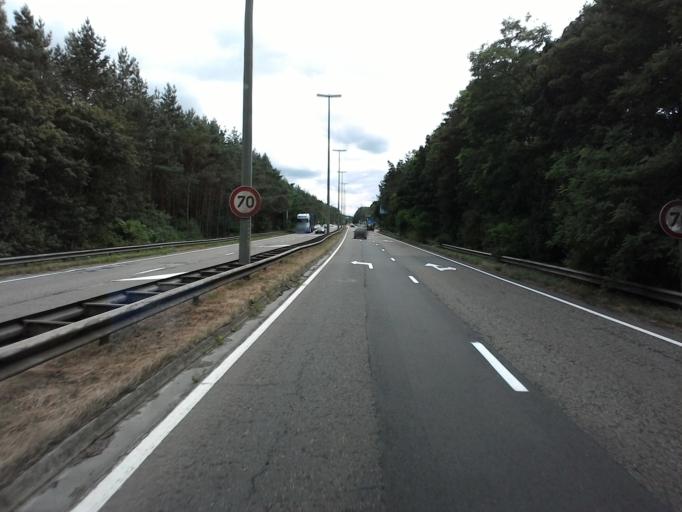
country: BE
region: Wallonia
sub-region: Province du Luxembourg
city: Arlon
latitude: 49.6754
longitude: 5.7788
